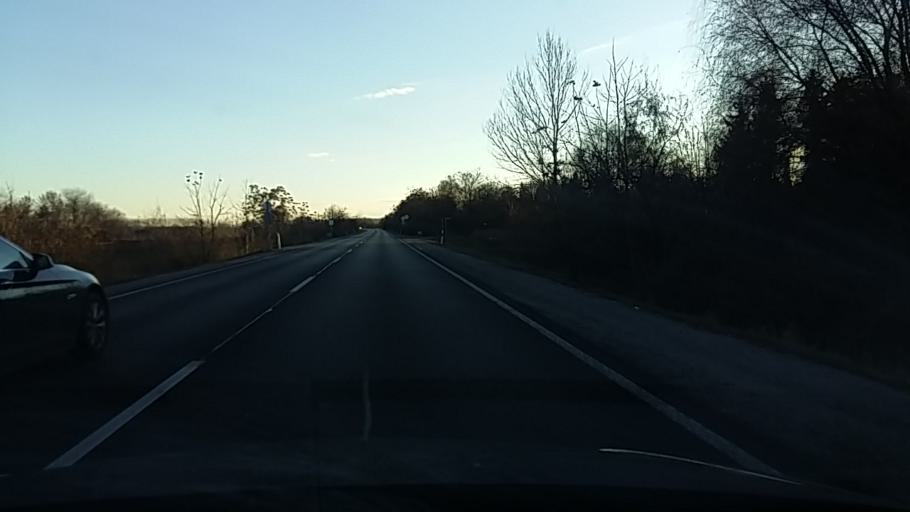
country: HU
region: Szabolcs-Szatmar-Bereg
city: Ujfeherto
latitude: 47.8603
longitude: 21.7044
